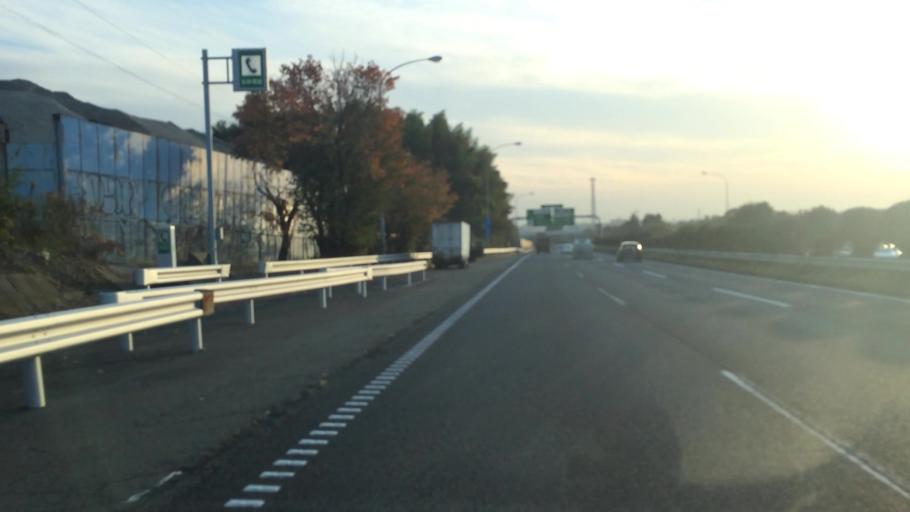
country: JP
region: Kanagawa
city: Yokohama
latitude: 35.5312
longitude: 139.5990
